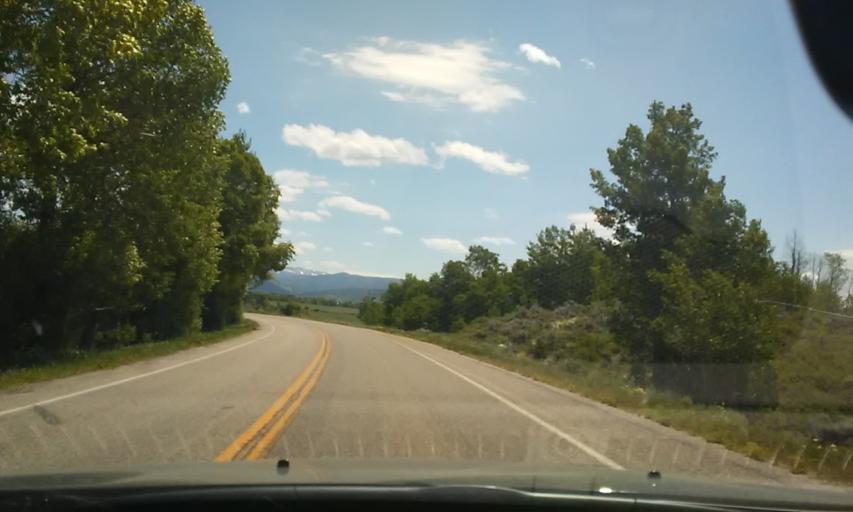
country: US
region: Wyoming
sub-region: Teton County
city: Jackson
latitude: 43.8382
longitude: -110.4830
